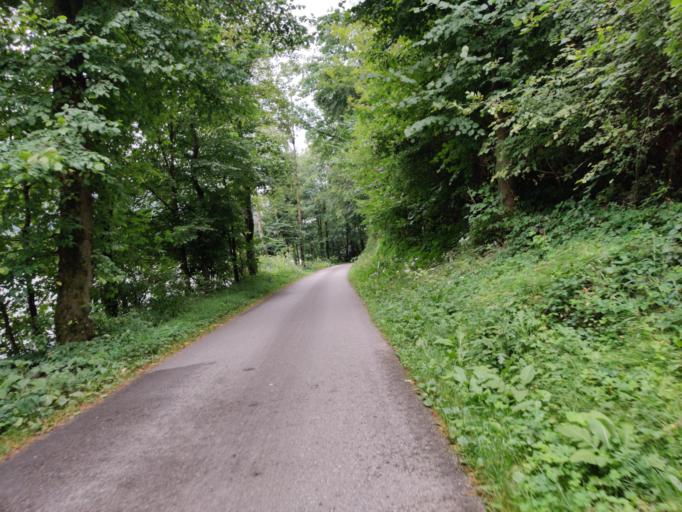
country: AT
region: Lower Austria
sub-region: Politischer Bezirk Melk
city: Nochling
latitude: 48.2186
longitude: 14.9484
